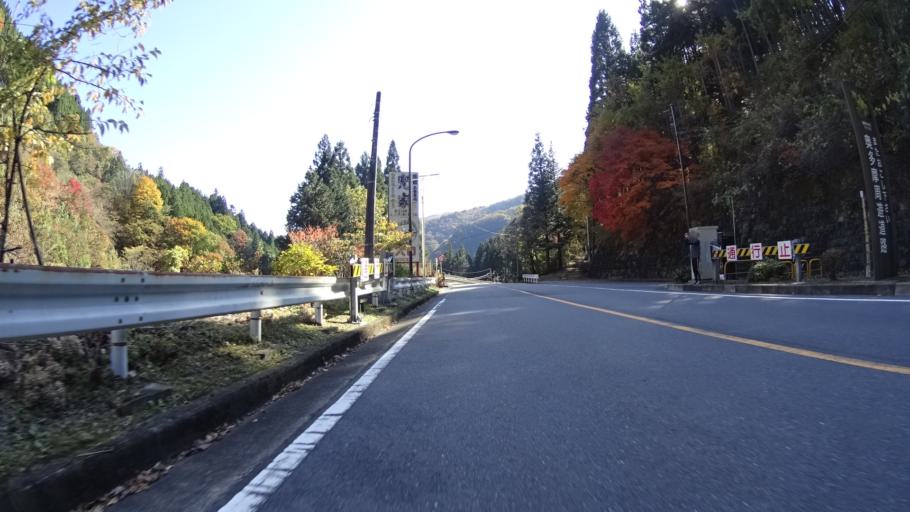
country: JP
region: Yamanashi
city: Uenohara
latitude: 35.7324
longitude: 139.0400
